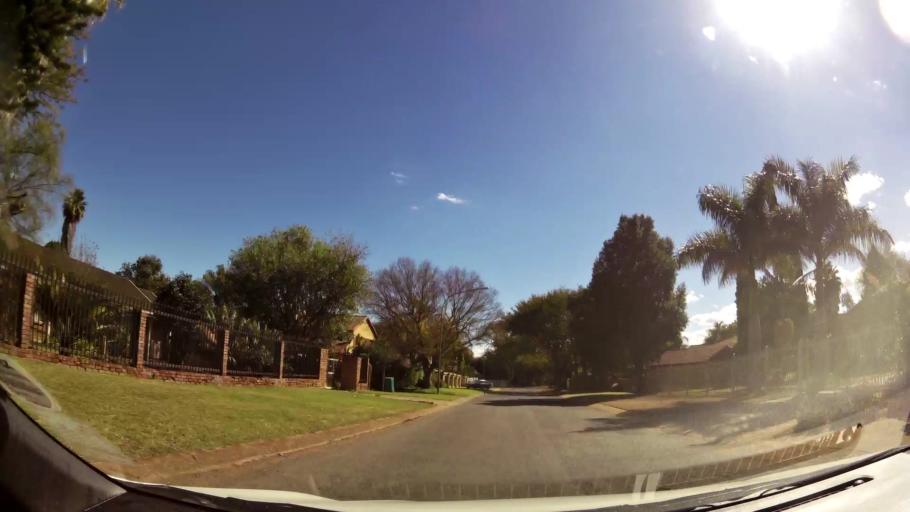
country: ZA
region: Limpopo
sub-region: Capricorn District Municipality
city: Polokwane
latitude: -23.9121
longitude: 29.4874
